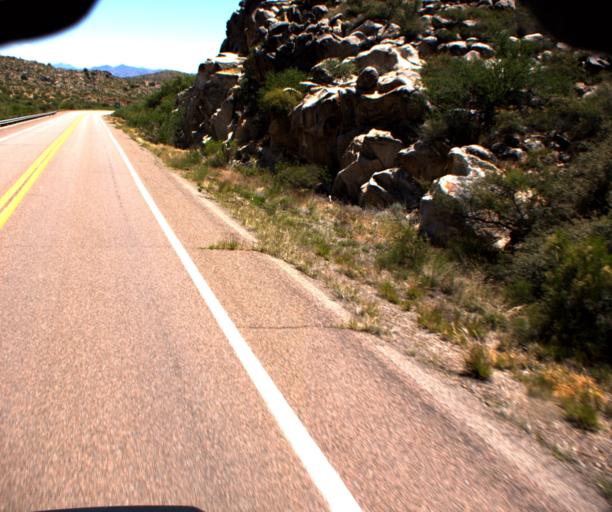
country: US
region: Arizona
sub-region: Yavapai County
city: Bagdad
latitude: 34.5326
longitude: -113.1411
